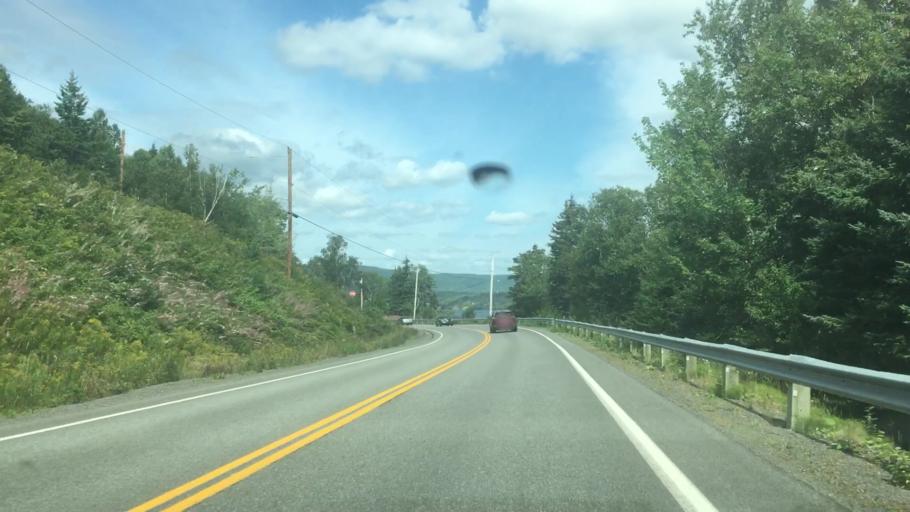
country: CA
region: Nova Scotia
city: Sydney Mines
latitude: 46.2716
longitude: -60.6095
